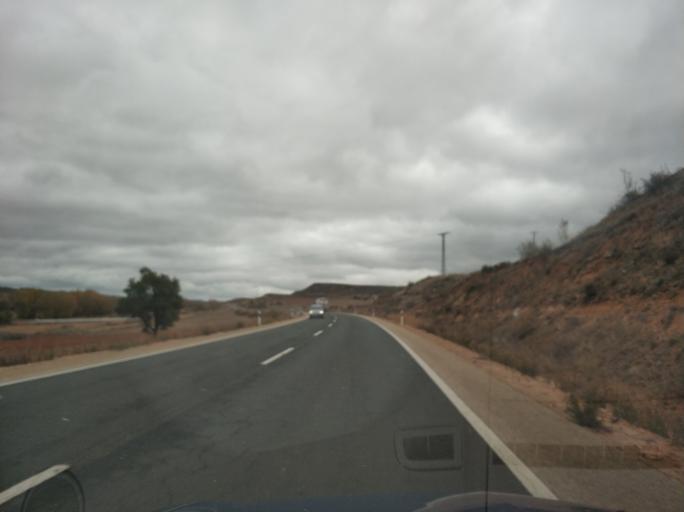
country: ES
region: Castille and Leon
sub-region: Provincia de Soria
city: San Esteban de Gormaz
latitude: 41.5796
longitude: -3.2196
